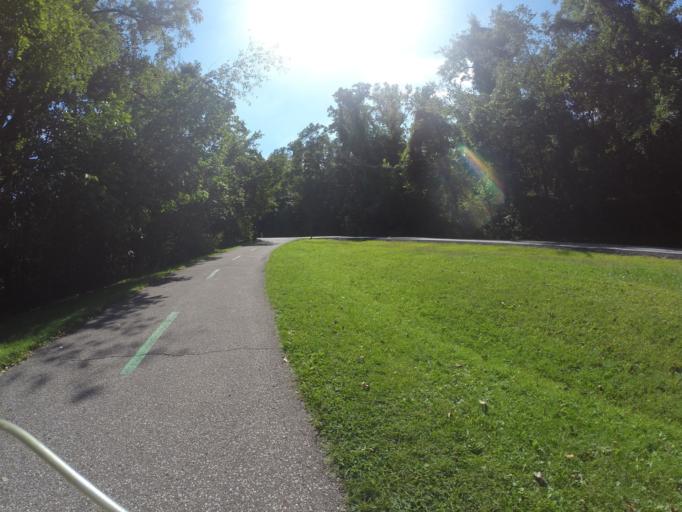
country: US
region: Ohio
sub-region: Cuyahoga County
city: South Euclid
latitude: 41.5404
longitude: -81.5245
